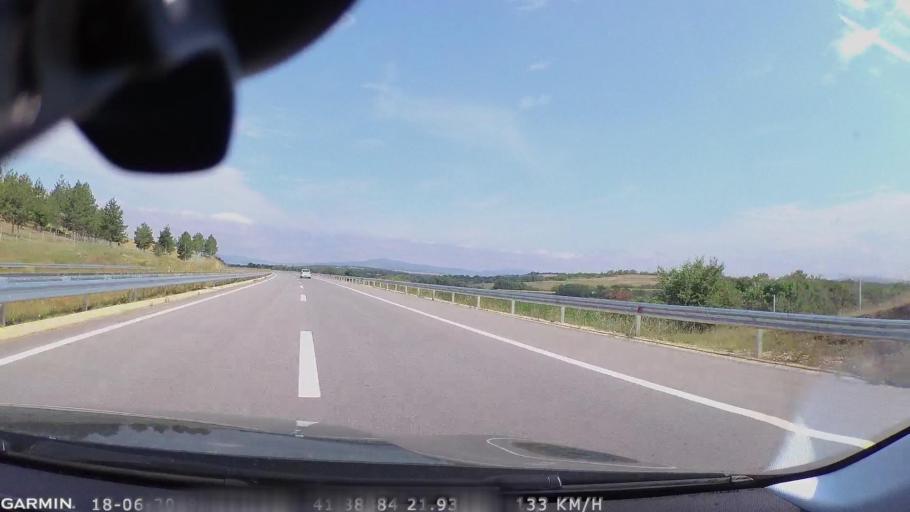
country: MK
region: Sveti Nikole
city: Sveti Nikole
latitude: 41.8899
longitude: 21.9296
